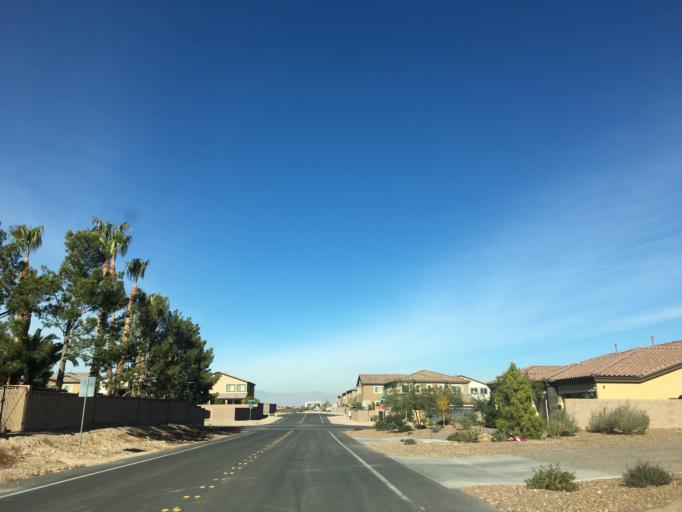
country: US
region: Nevada
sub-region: Clark County
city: Enterprise
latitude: 36.0037
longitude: -115.1856
